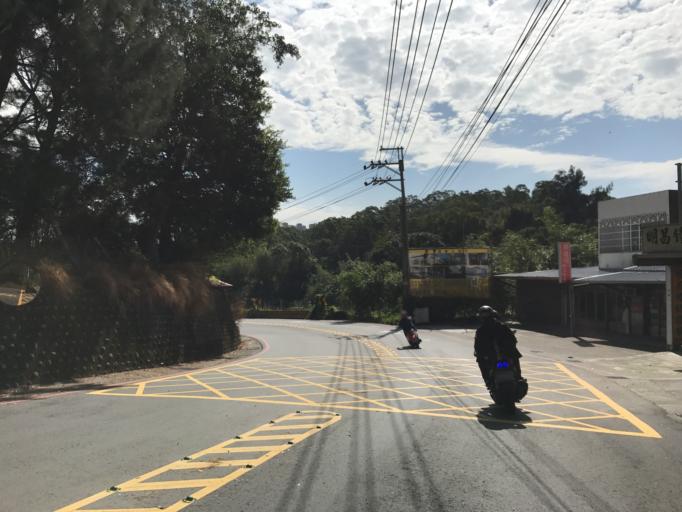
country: TW
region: Taiwan
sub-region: Hsinchu
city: Hsinchu
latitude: 24.7705
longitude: 120.9734
